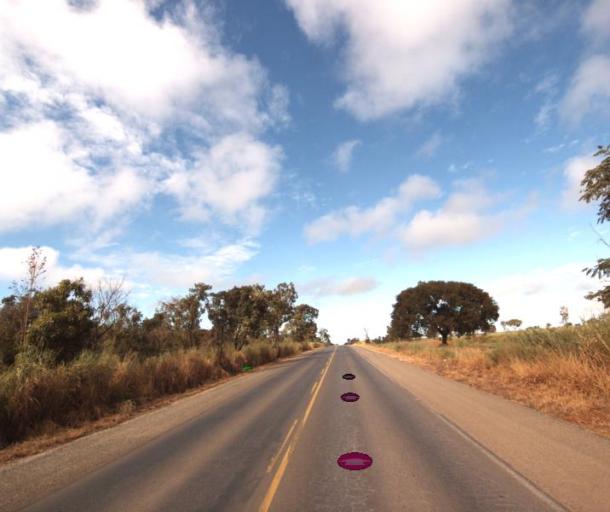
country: BR
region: Goias
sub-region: Uruacu
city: Uruacu
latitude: -14.7897
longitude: -49.2781
